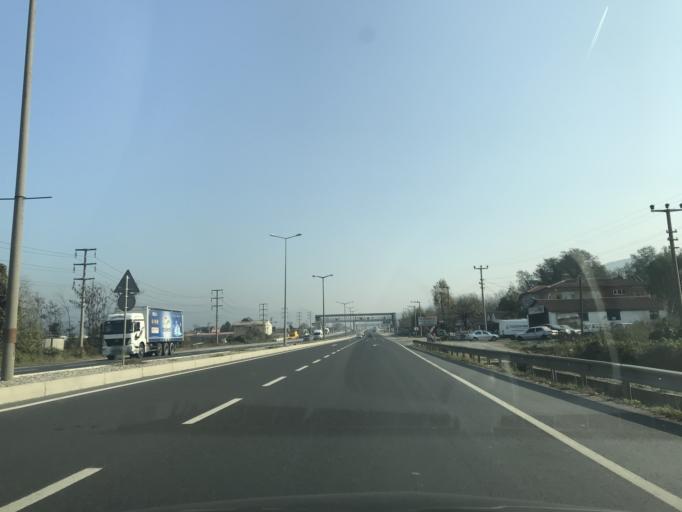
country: TR
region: Duzce
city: Kaynasli
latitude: 40.7780
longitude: 31.2924
